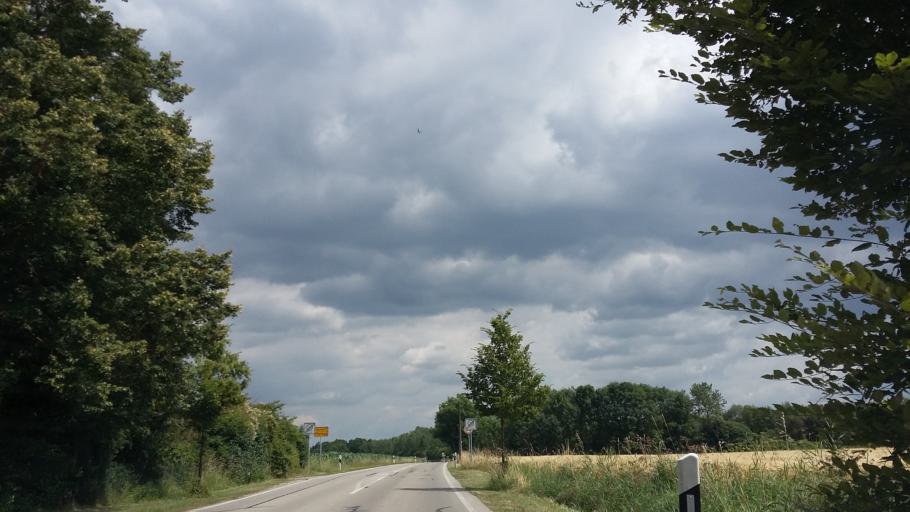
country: DE
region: Bavaria
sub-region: Upper Bavaria
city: Planegg
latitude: 48.1012
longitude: 11.4329
